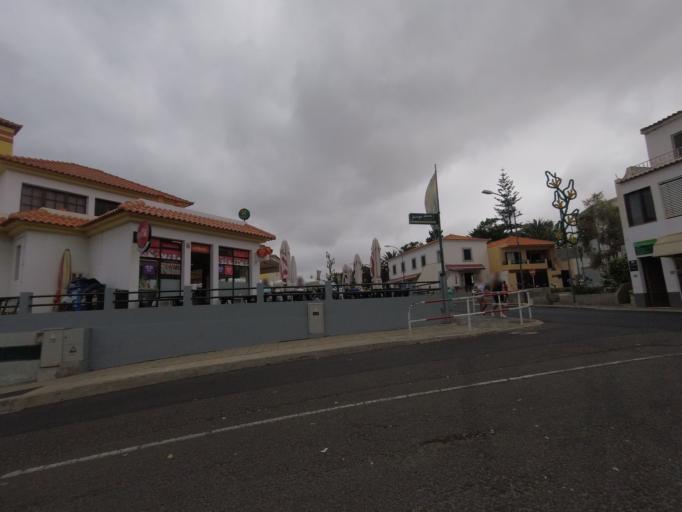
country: PT
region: Madeira
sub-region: Porto Santo
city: Vila de Porto Santo
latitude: 33.0589
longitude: -16.3342
